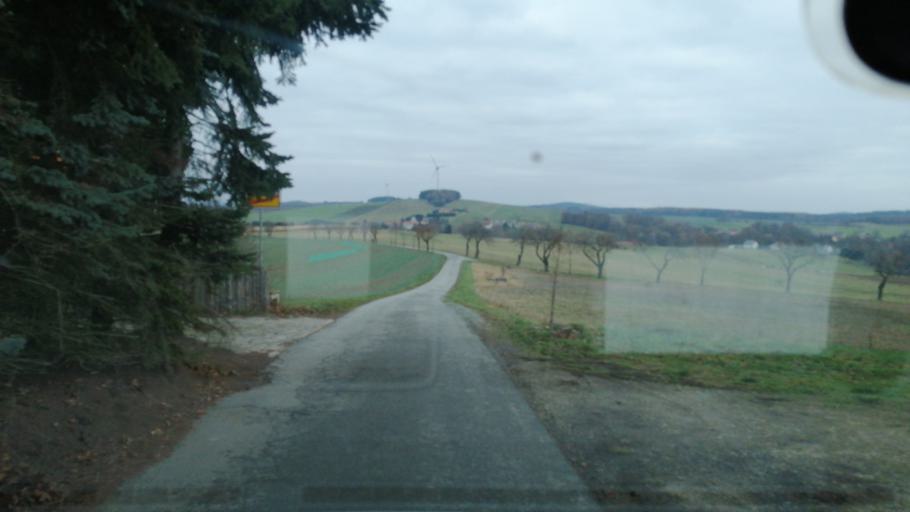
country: DE
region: Saxony
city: Bernstadt
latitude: 51.0561
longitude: 14.7978
